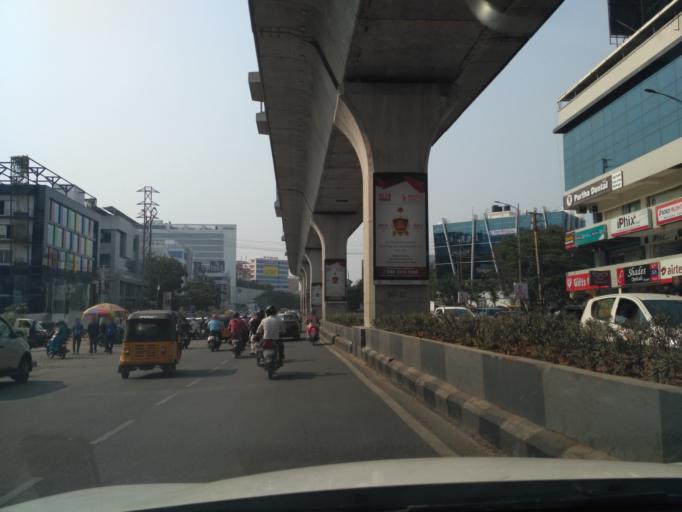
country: IN
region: Telangana
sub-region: Rangareddi
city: Kukatpalli
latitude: 17.4452
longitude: 78.3861
